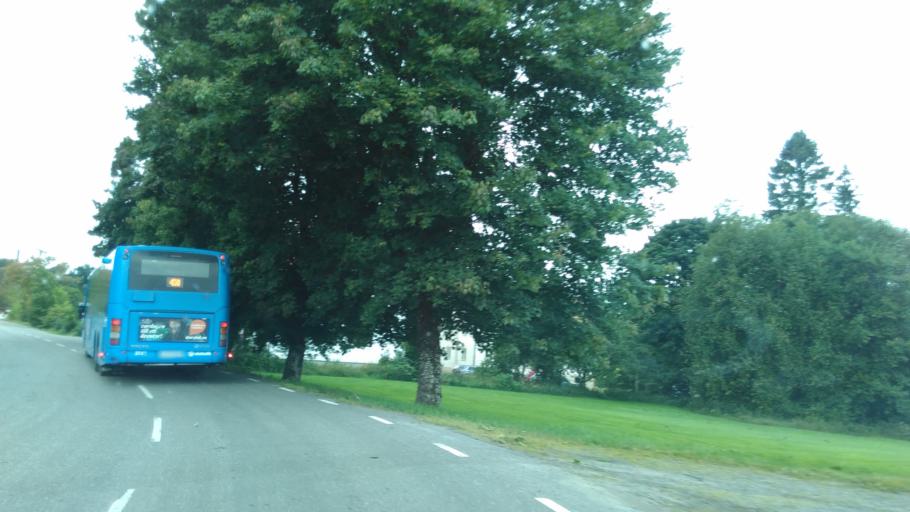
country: SE
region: Vaestra Goetaland
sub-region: Marks Kommun
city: Fritsla
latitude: 57.5601
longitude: 12.7905
